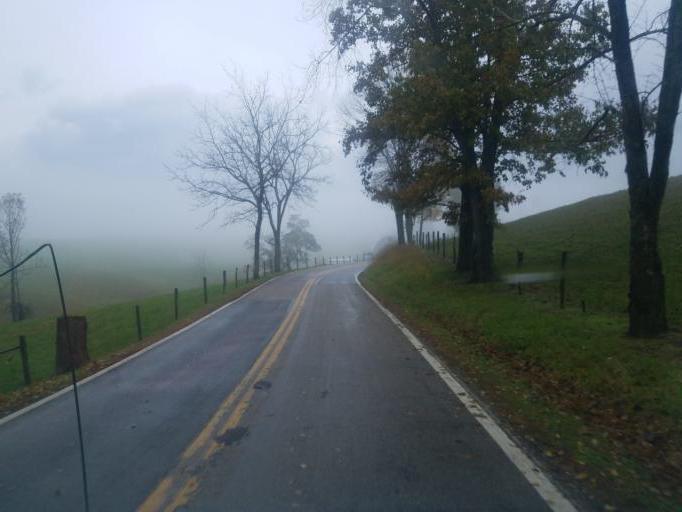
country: US
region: Ohio
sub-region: Morgan County
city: McConnelsville
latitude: 39.5142
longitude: -81.9173
